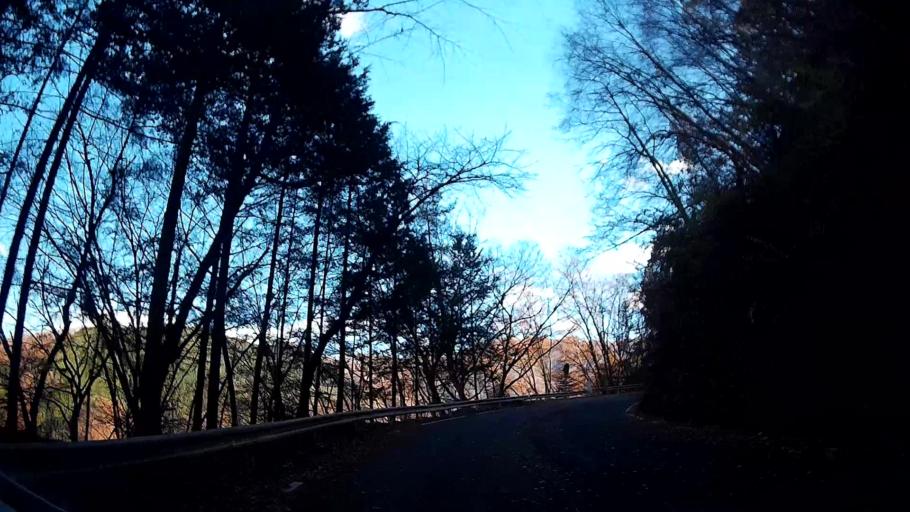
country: JP
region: Yamanashi
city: Otsuki
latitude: 35.7427
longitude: 138.9601
